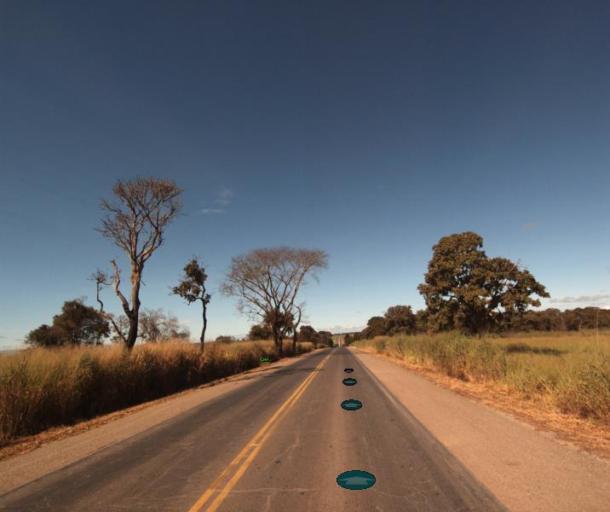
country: BR
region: Goias
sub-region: Itapaci
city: Itapaci
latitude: -14.9058
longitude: -49.3514
